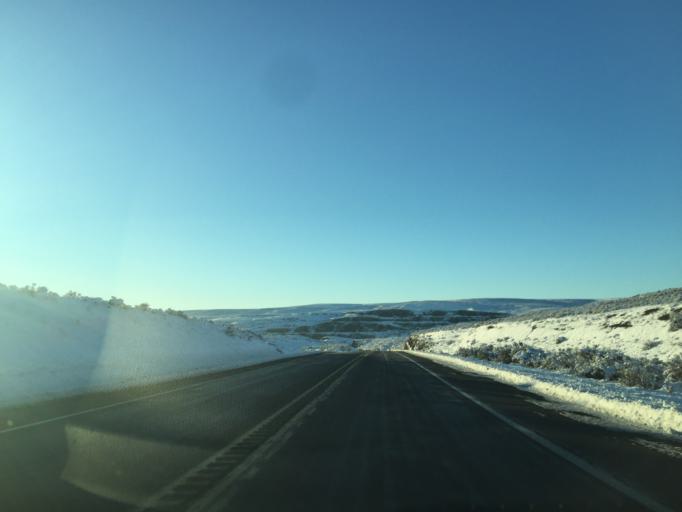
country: US
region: Washington
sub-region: Grant County
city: Soap Lake
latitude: 47.6069
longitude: -119.6548
